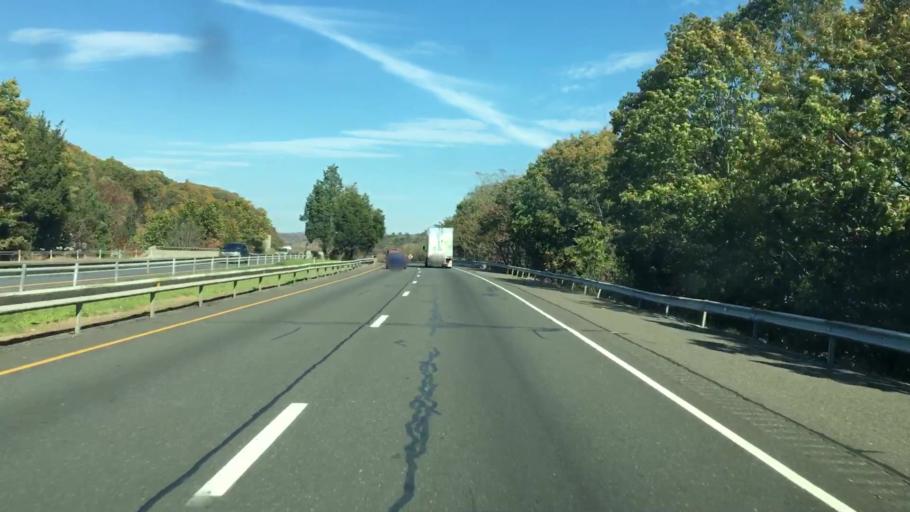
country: US
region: Connecticut
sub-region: New Haven County
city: Ansonia
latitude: 41.3676
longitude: -73.0877
